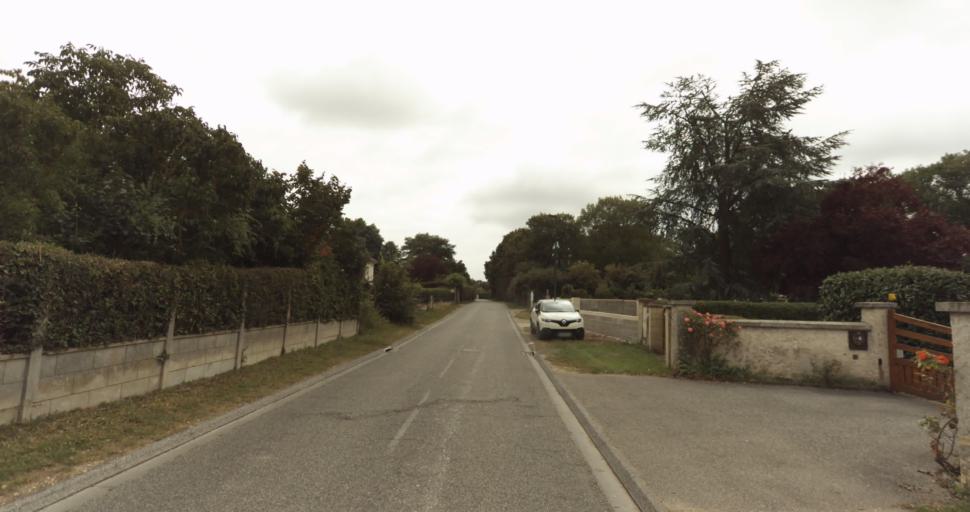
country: FR
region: Haute-Normandie
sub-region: Departement de l'Eure
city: Garennes-sur-Eure
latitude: 48.9110
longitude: 1.4451
